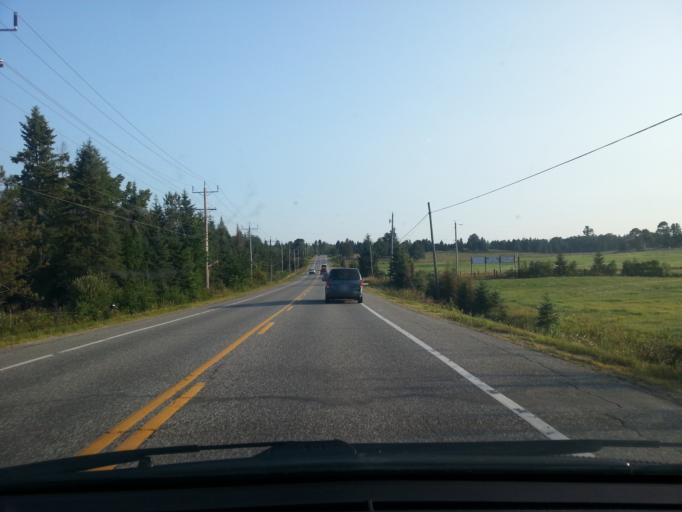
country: CA
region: Quebec
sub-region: Outaouais
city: Wakefield
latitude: 45.9198
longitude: -76.0171
